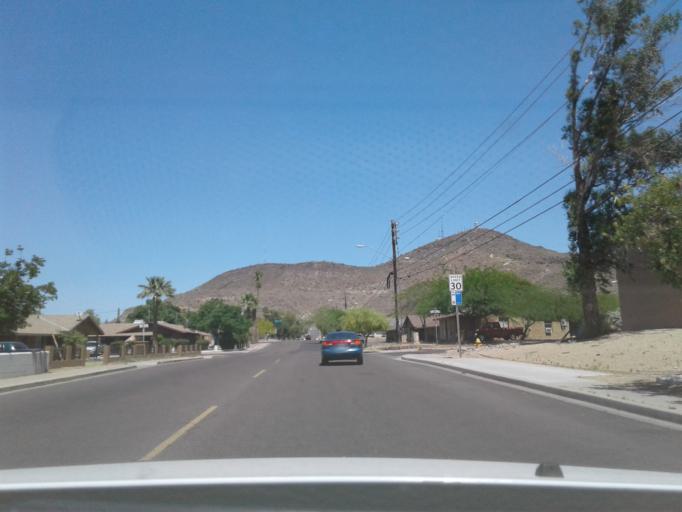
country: US
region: Arizona
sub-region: Maricopa County
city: Glendale
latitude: 33.5798
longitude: -112.0913
